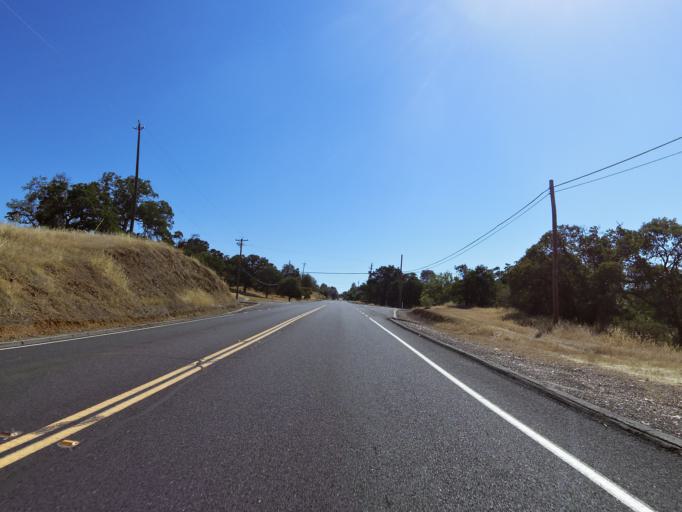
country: US
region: California
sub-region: Tuolumne County
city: Jamestown
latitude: 37.7117
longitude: -120.3297
